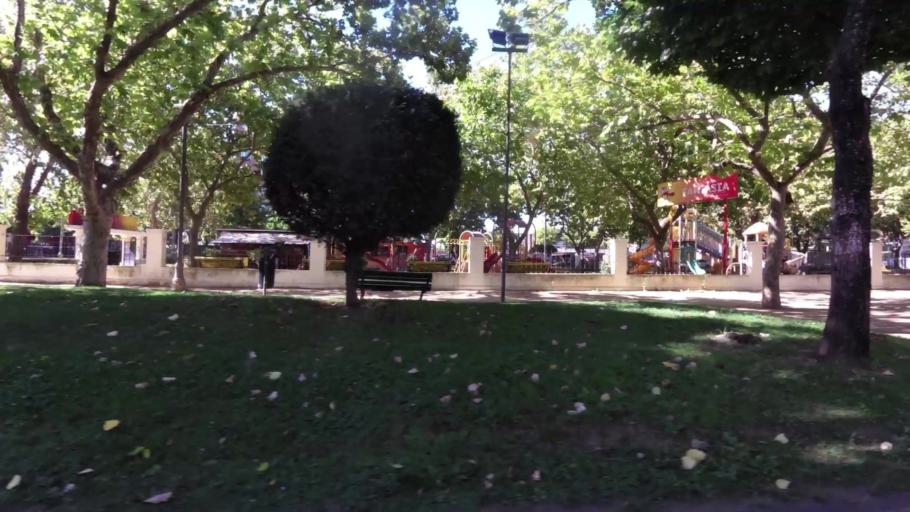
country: CL
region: Maule
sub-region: Provincia de Talca
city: Talca
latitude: -35.4224
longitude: -71.6617
